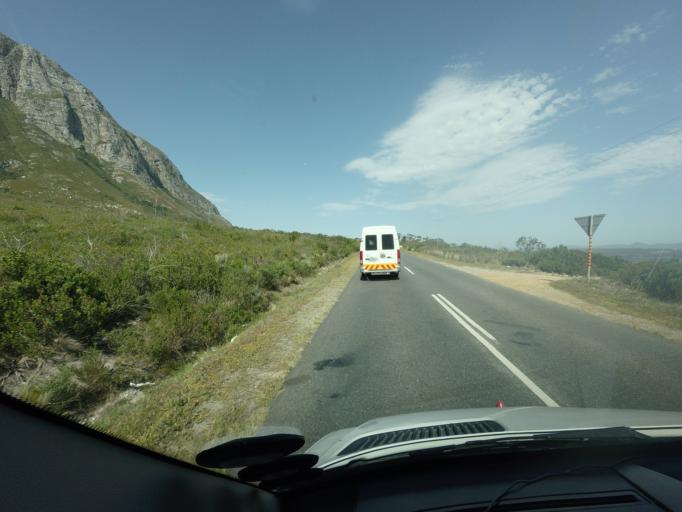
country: ZA
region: Western Cape
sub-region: Overberg District Municipality
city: Hermanus
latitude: -34.4057
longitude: 19.3357
